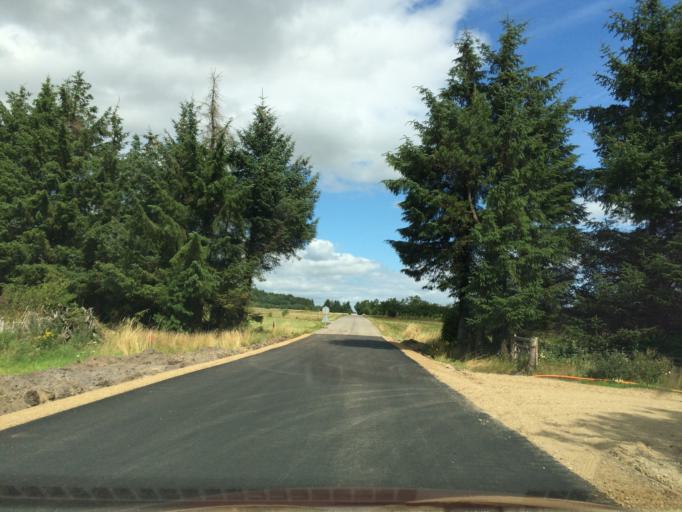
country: DK
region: Central Jutland
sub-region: Silkeborg Kommune
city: Svejbaek
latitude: 56.1839
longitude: 9.6402
